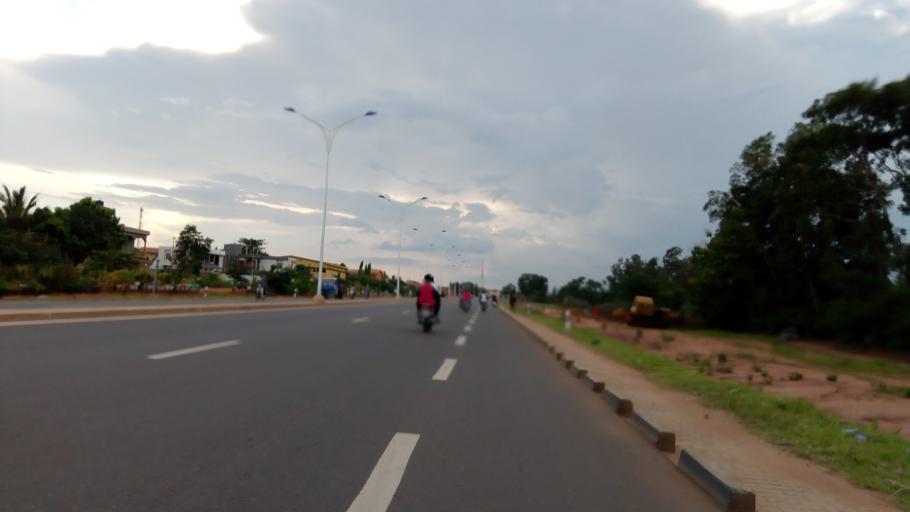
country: TG
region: Maritime
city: Lome
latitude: 6.2447
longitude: 1.1892
